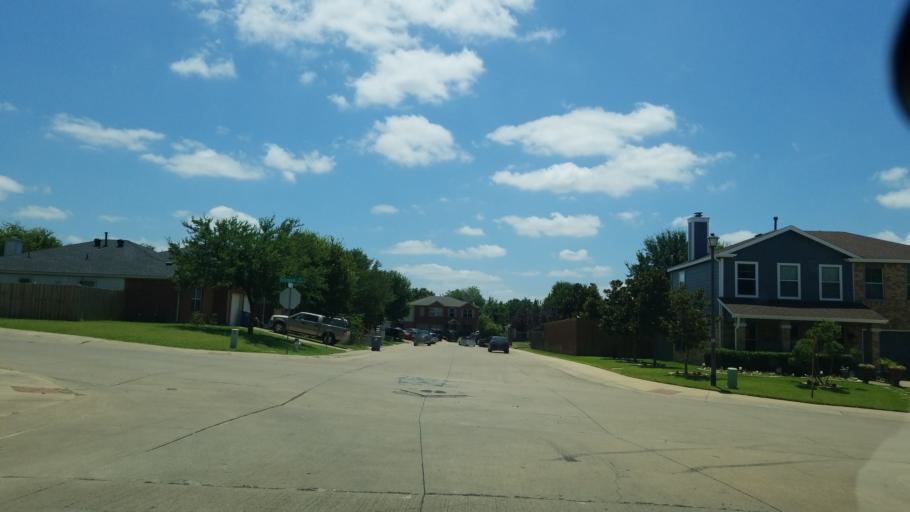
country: US
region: Texas
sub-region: Dallas County
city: Balch Springs
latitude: 32.7448
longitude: -96.7008
